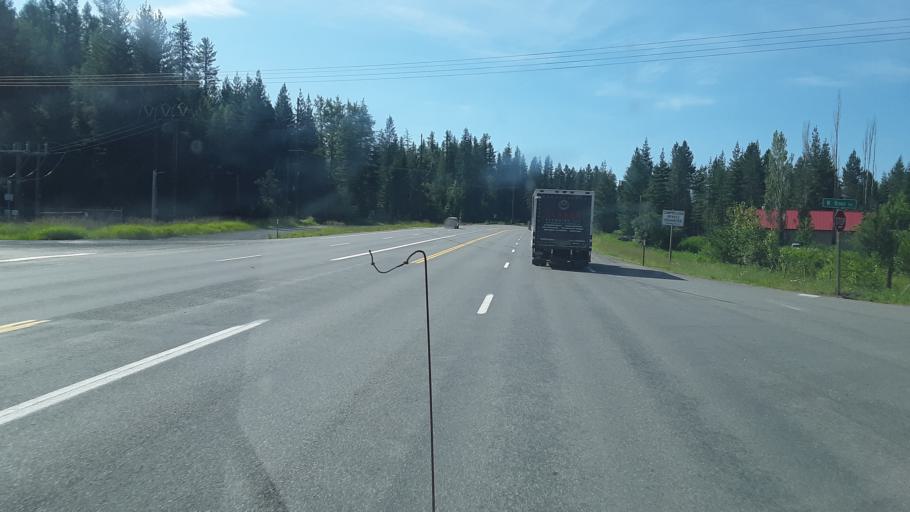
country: US
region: Idaho
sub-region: Bonner County
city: Ponderay
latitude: 48.3285
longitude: -116.5474
